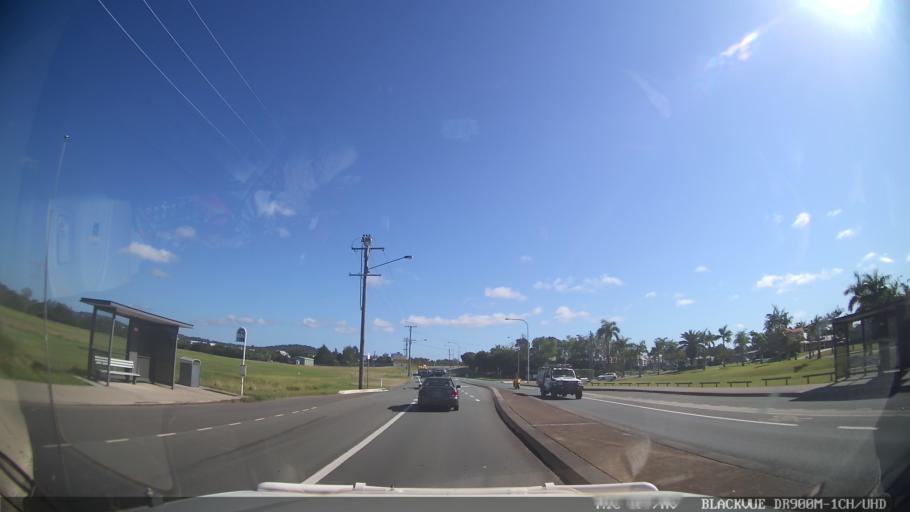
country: AU
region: Queensland
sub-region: Sunshine Coast
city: Twin Waters
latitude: -26.6328
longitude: 153.0382
